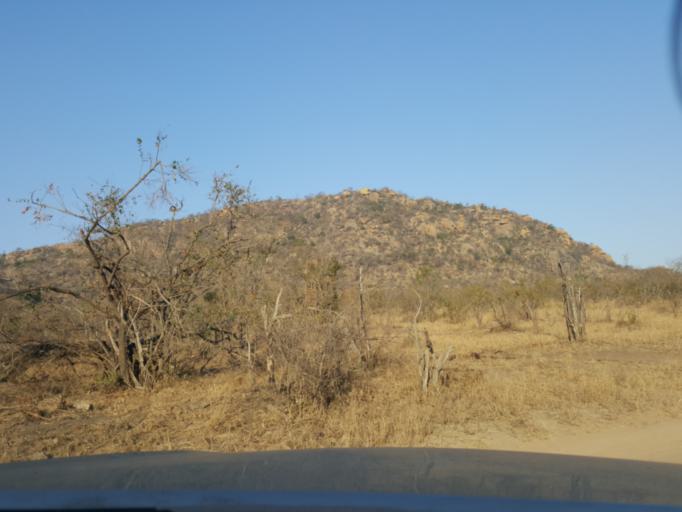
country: ZA
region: Mpumalanga
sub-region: Ehlanzeni District
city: White River
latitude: -25.4024
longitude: 31.4372
